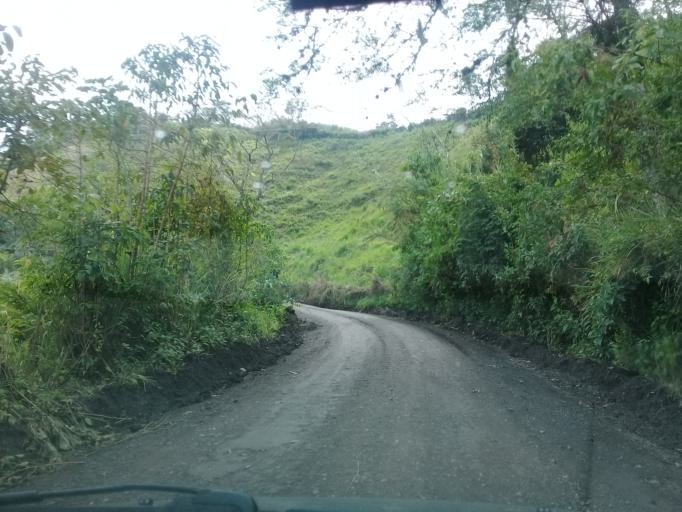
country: CO
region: Cundinamarca
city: Quipile
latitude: 4.7139
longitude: -74.5316
